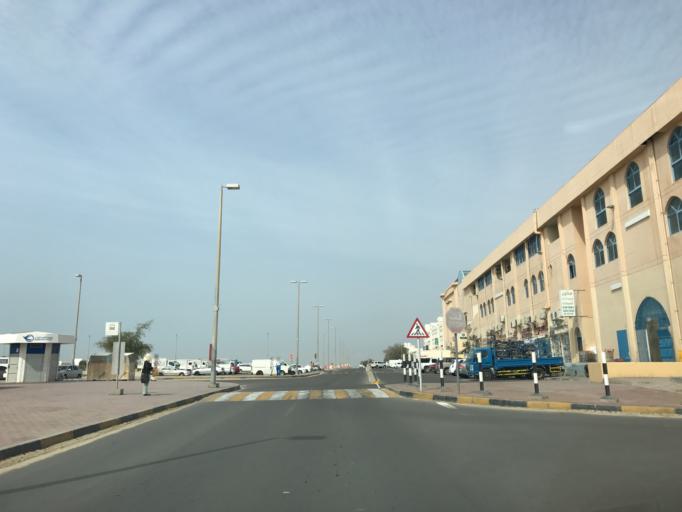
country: AE
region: Abu Dhabi
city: Abu Dhabi
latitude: 24.5547
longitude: 54.6939
